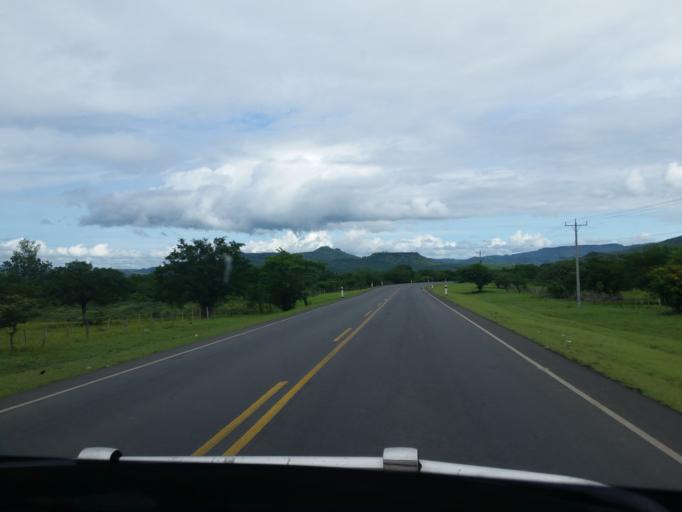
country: NI
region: Managua
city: Tipitapa
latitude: 12.4027
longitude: -86.0433
